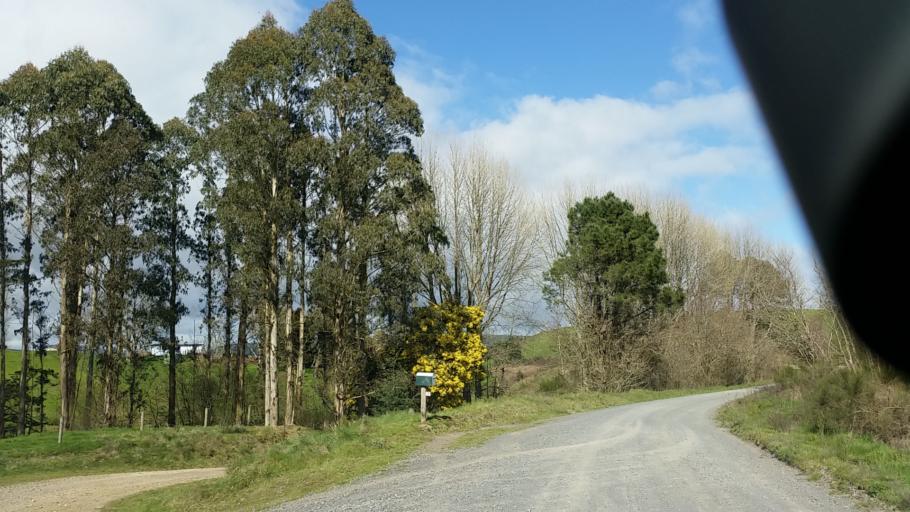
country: NZ
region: Waikato
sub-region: South Waikato District
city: Tokoroa
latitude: -38.3834
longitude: 176.0814
